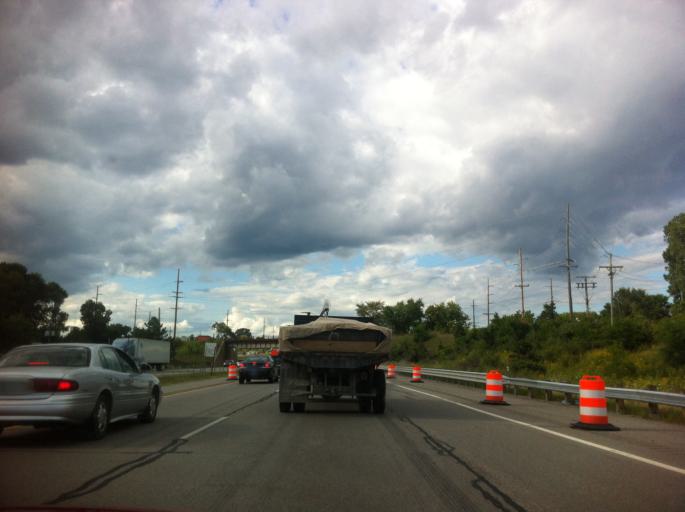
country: US
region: Michigan
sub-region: Livingston County
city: Brighton
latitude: 42.5098
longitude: -83.7581
